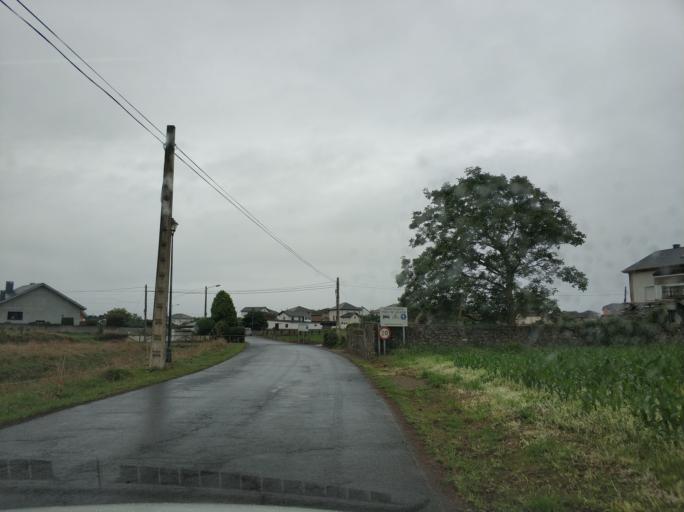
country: ES
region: Asturias
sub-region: Province of Asturias
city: Tineo
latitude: 43.5546
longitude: -6.4616
